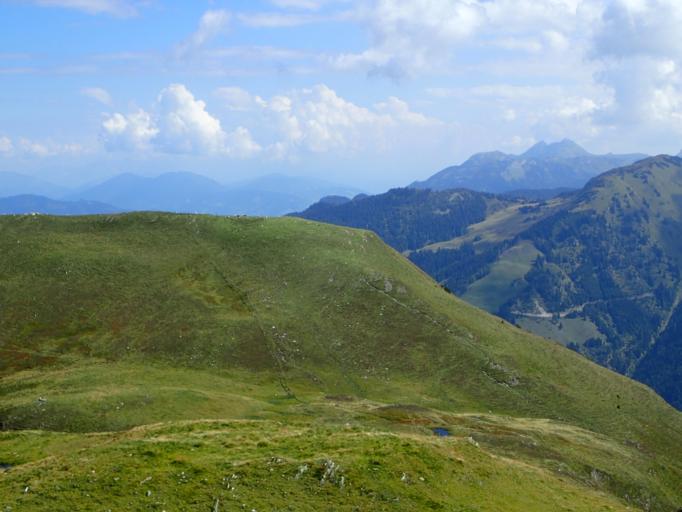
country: AT
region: Salzburg
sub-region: Politischer Bezirk Zell am See
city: Taxenbach
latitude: 47.2433
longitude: 12.9501
